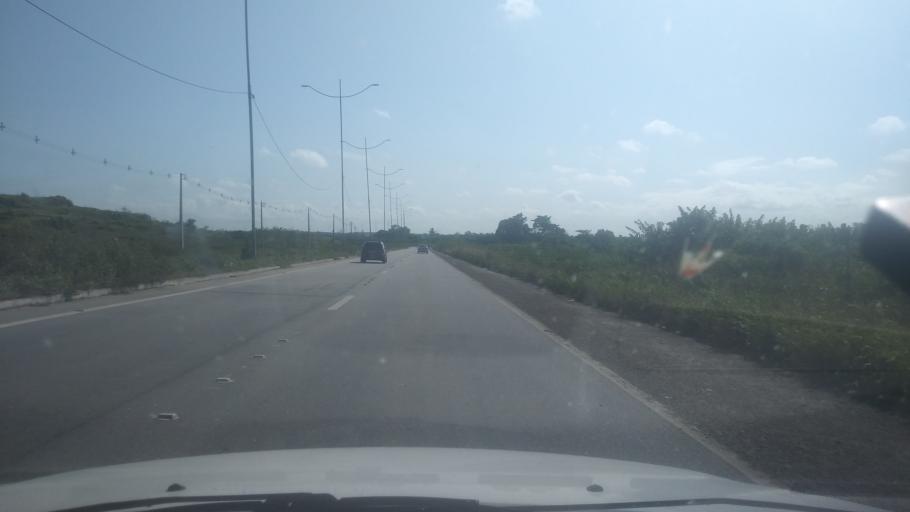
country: BR
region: Rio Grande do Norte
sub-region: Macaiba
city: Macaiba
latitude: -5.8175
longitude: -35.3642
